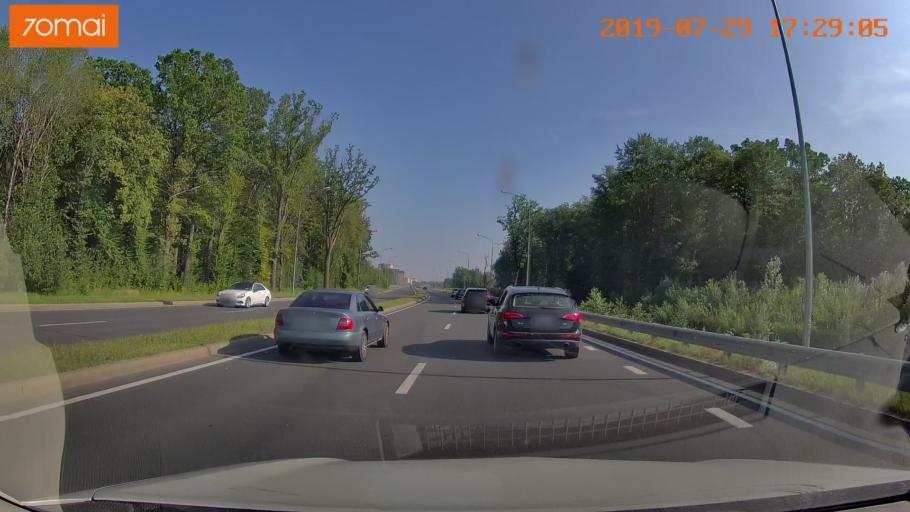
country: RU
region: Kaliningrad
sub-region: Gorod Kaliningrad
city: Kaliningrad
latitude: 54.7577
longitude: 20.4712
